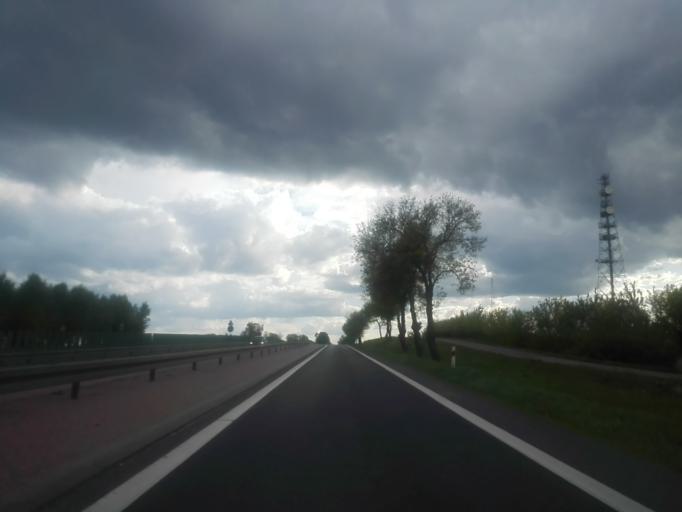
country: PL
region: Masovian Voivodeship
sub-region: Powiat ostrowski
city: Ostrow Mazowiecka
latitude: 52.8250
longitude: 21.9328
